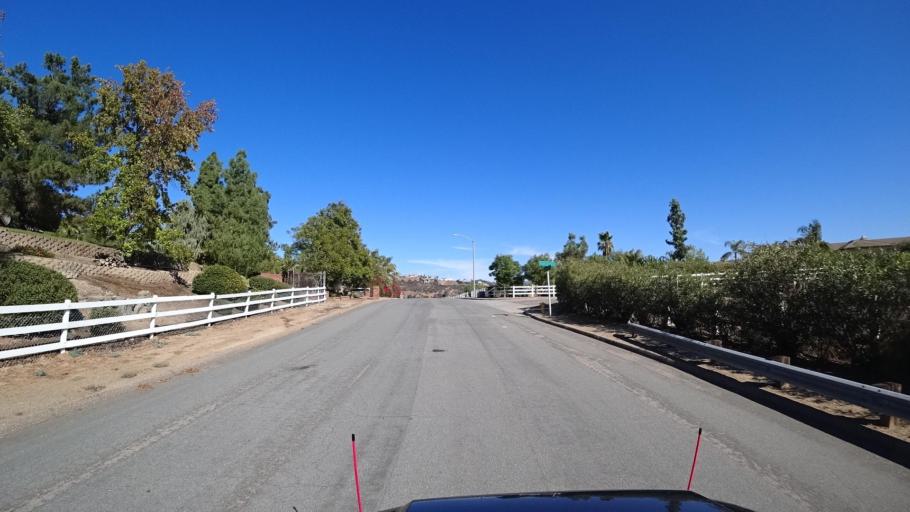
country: US
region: California
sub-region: San Diego County
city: Lakeside
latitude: 32.8656
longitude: -116.8793
